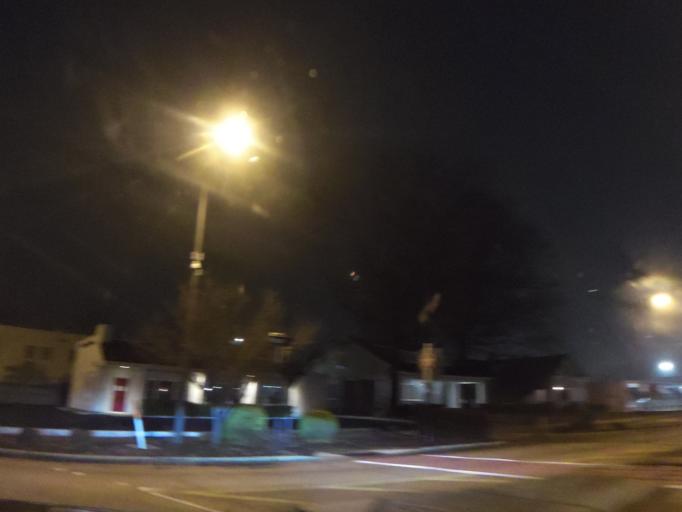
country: US
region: North Carolina
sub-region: Cumberland County
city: Fayetteville
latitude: 35.0511
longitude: -78.8743
